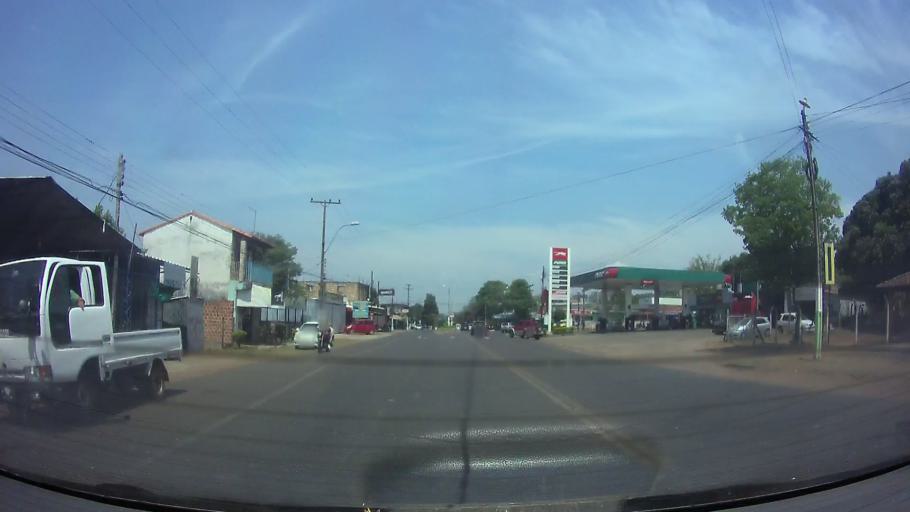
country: PY
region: Central
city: Guarambare
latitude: -25.4462
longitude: -57.4389
